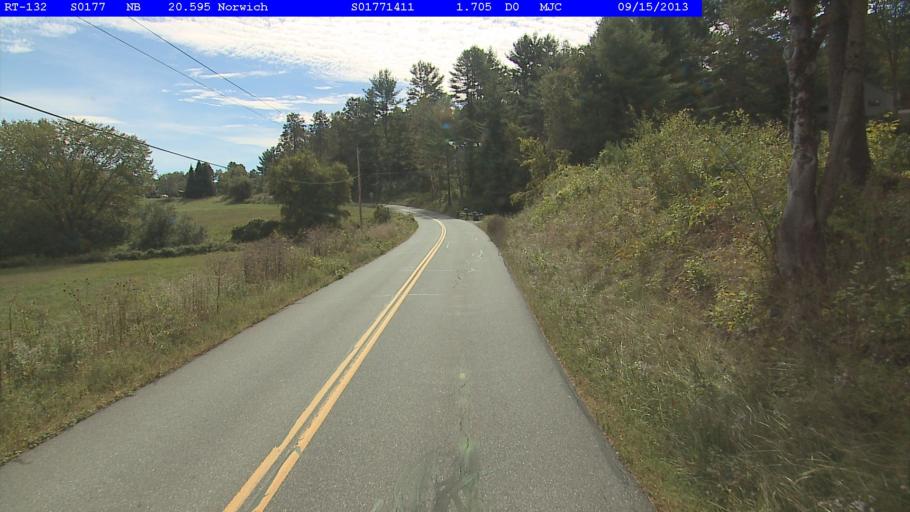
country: US
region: New Hampshire
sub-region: Grafton County
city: Hanover
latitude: 43.7667
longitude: -72.2454
